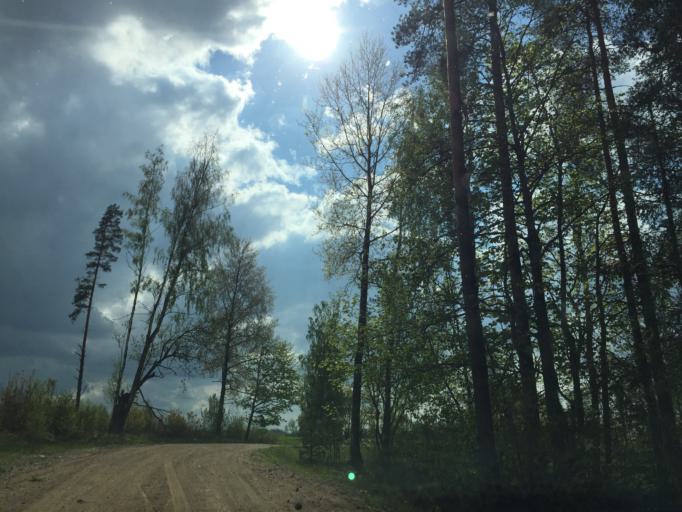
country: LV
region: Sigulda
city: Sigulda
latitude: 57.2939
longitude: 24.8268
